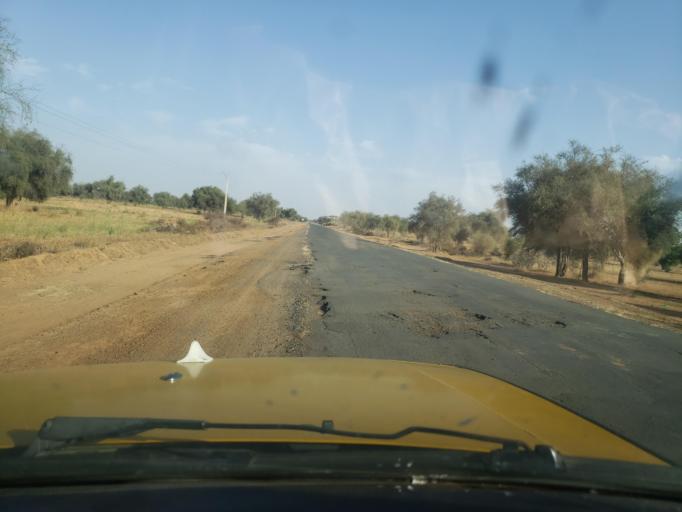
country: SN
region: Louga
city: Louga
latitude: 15.5026
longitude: -15.9456
